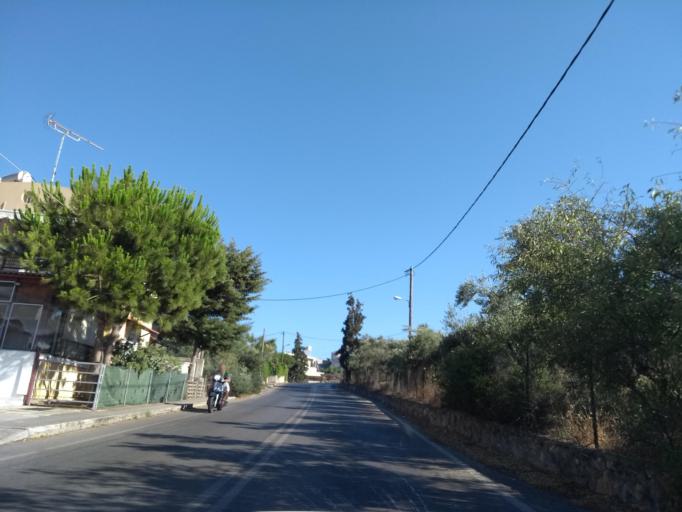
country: GR
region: Crete
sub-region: Nomos Chanias
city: Pithari
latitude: 35.5366
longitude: 24.0814
